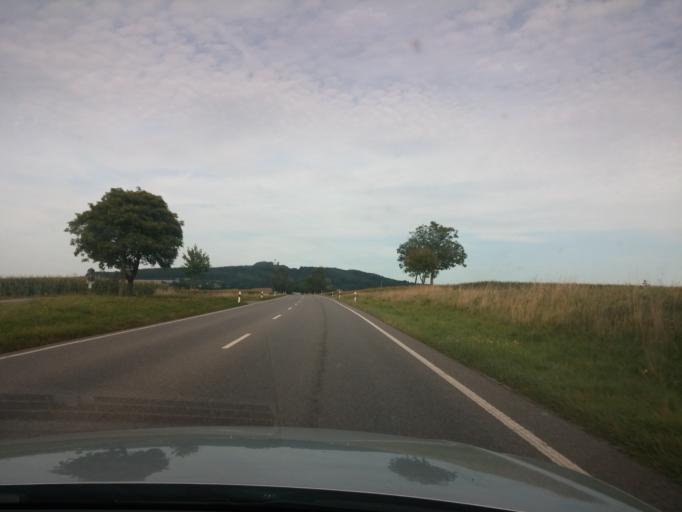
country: DE
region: Baden-Wuerttemberg
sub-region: Tuebingen Region
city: Unlingen
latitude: 48.1530
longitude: 9.5145
